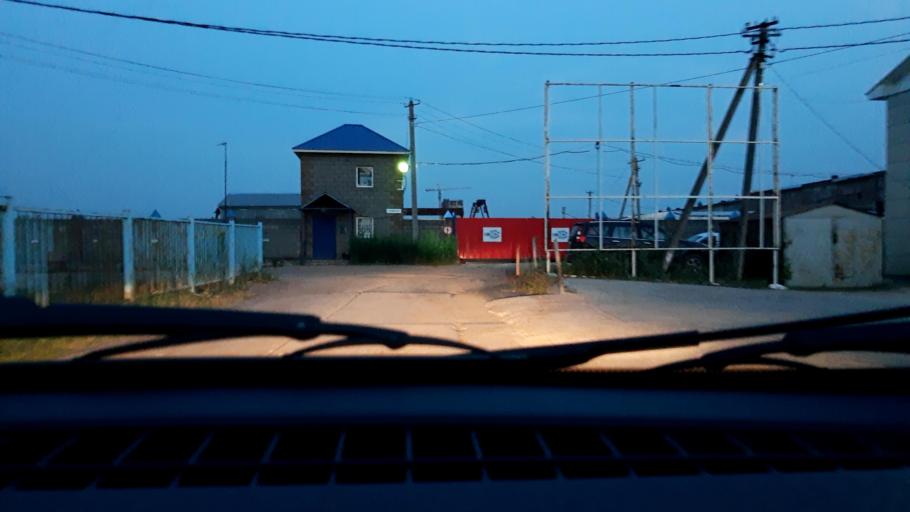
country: RU
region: Bashkortostan
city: Mikhaylovka
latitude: 54.8034
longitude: 55.8729
